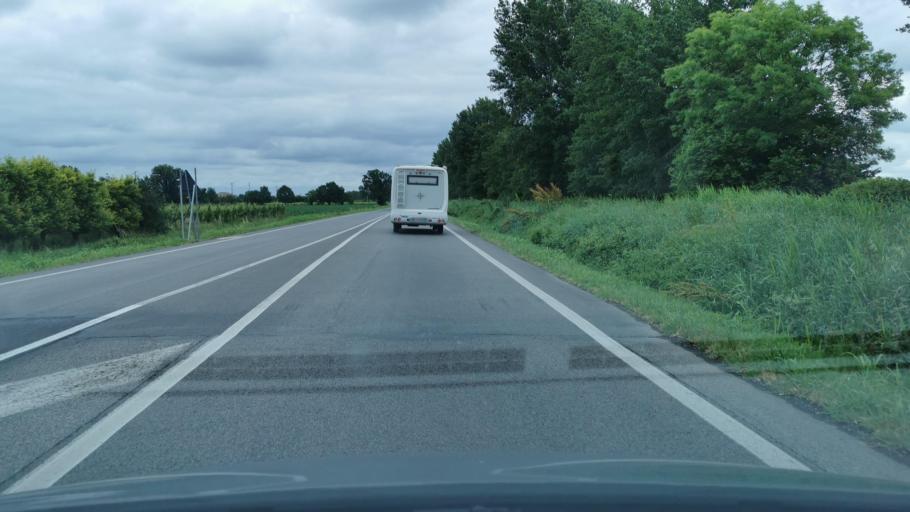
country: IT
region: Emilia-Romagna
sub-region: Provincia di Ravenna
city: Granarolo
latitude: 44.3447
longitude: 11.9230
